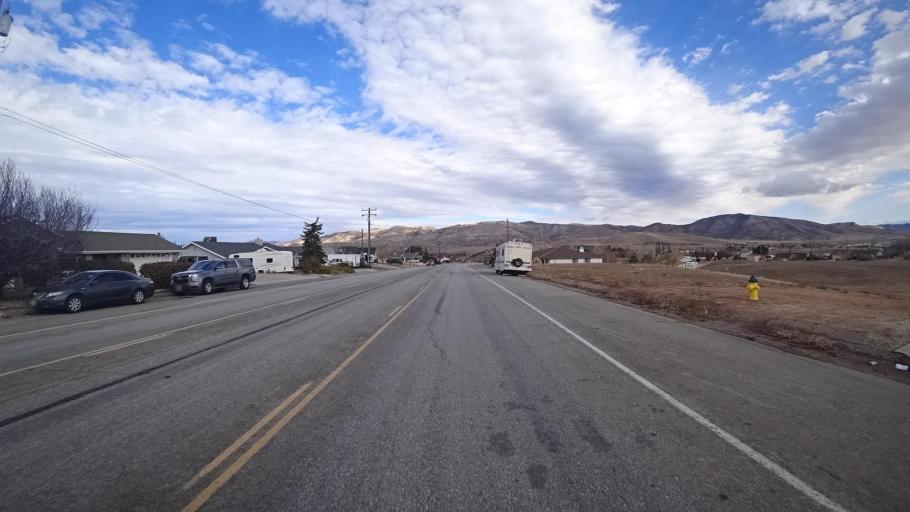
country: US
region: California
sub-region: Kern County
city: Golden Hills
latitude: 35.1313
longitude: -118.4815
